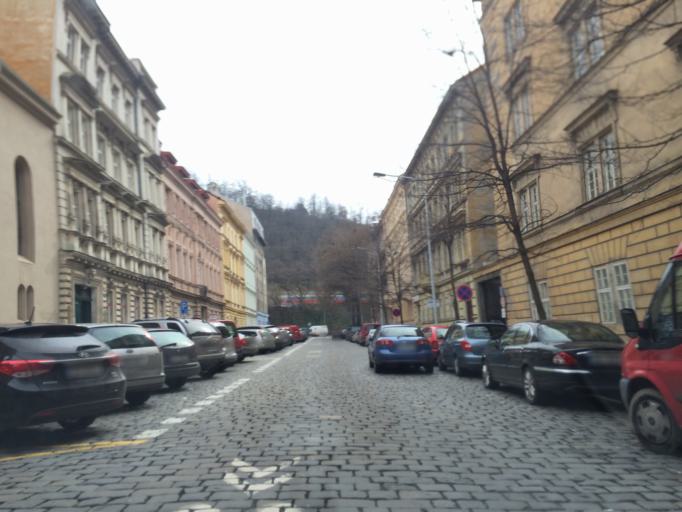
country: CZ
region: Praha
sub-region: Praha 8
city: Karlin
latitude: 50.0907
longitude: 14.4456
